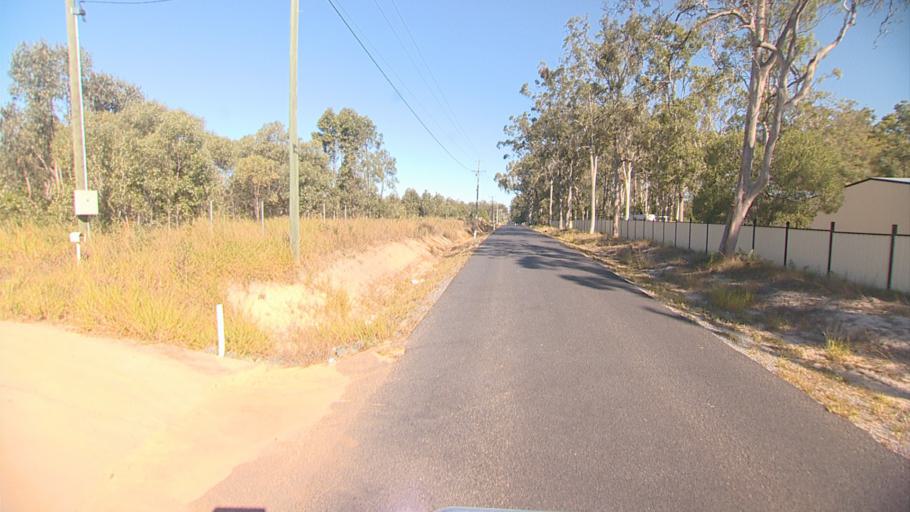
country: AU
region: Queensland
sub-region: Logan
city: Logan Reserve
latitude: -27.7219
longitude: 153.0738
